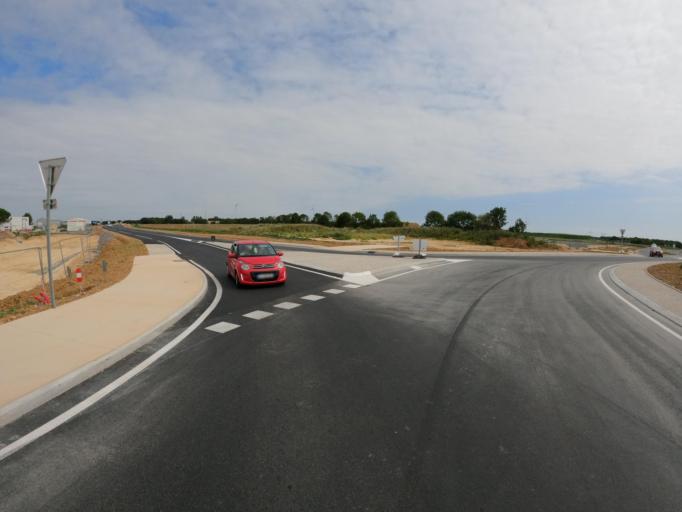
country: FR
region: Poitou-Charentes
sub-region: Departement de la Charente-Maritime
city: Saint-Jean-de-Liversay
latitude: 46.2293
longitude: -0.8793
